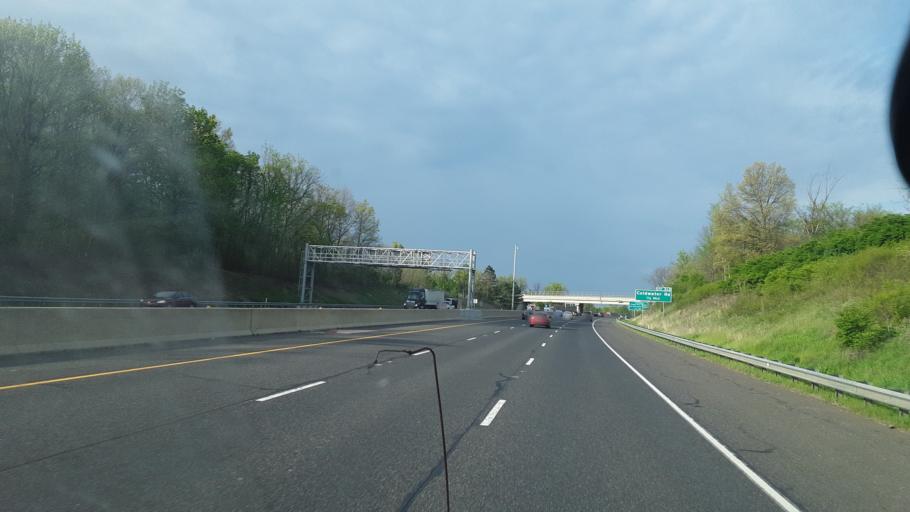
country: US
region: Indiana
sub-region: Allen County
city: Fort Wayne
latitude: 41.1504
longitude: -85.1145
